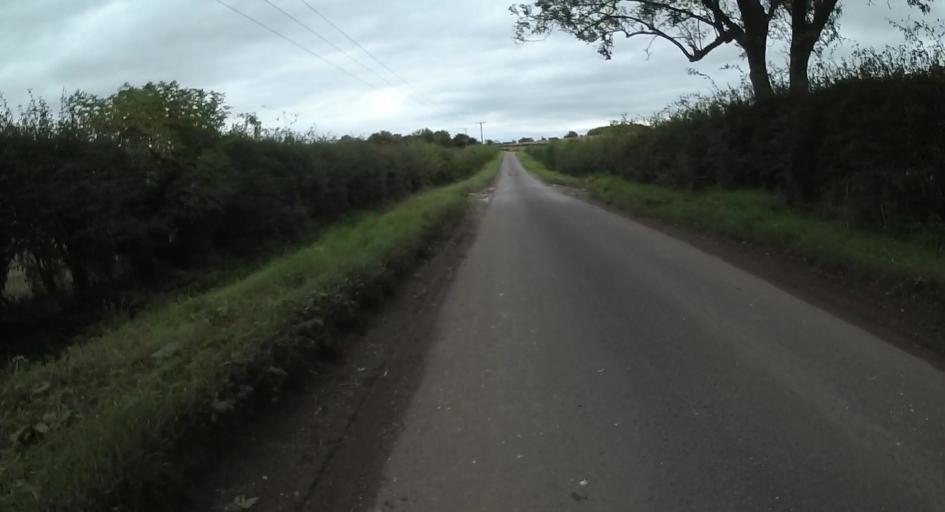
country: GB
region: England
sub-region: Hampshire
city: Four Marks
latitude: 51.1592
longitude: -1.1199
